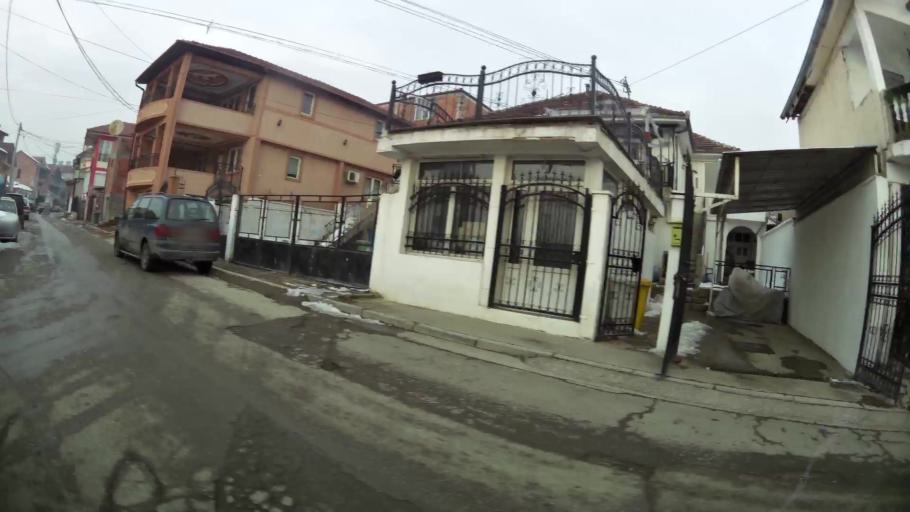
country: MK
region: Suto Orizari
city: Suto Orizare
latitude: 42.0402
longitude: 21.4256
